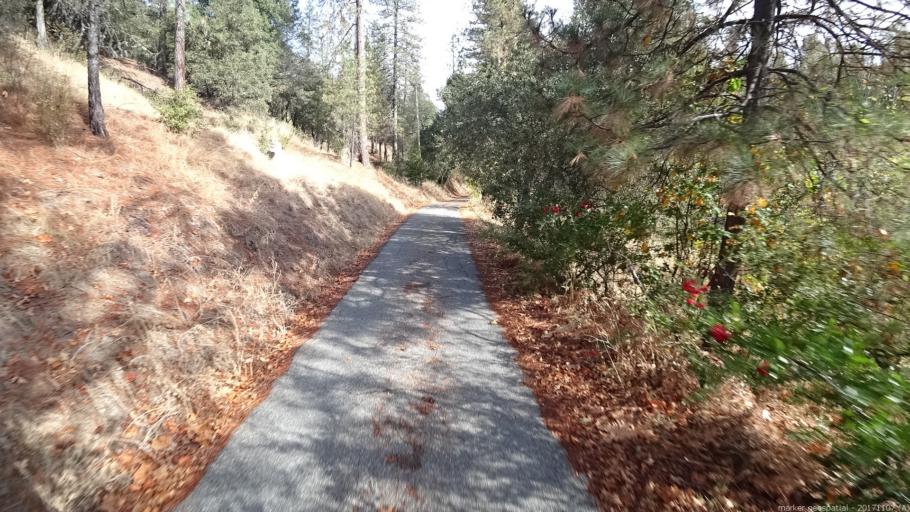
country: US
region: California
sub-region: Shasta County
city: Shasta
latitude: 40.5422
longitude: -122.5815
